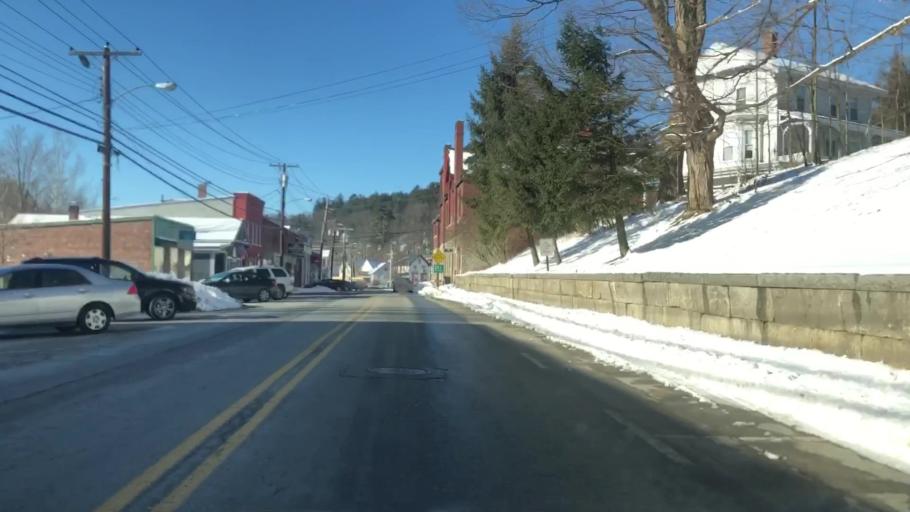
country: US
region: New Hampshire
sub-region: Hillsborough County
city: Wilton
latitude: 42.8431
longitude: -71.7372
